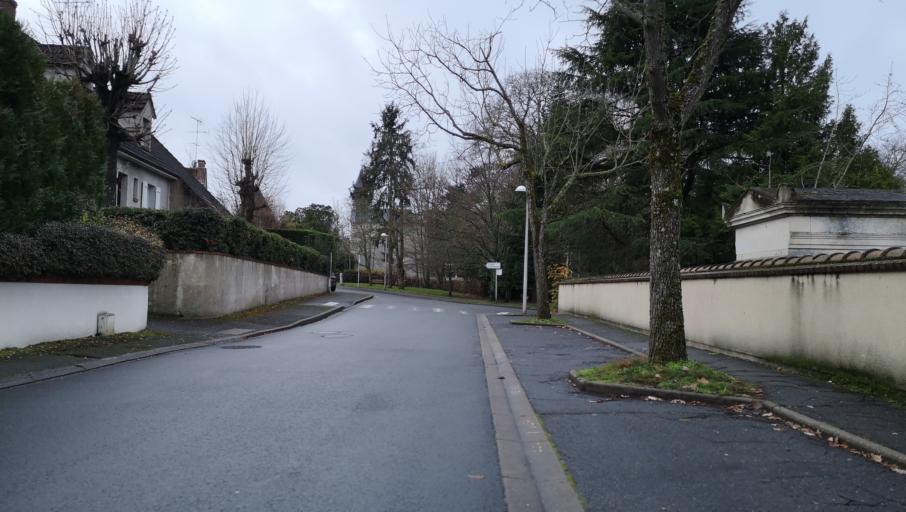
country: FR
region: Centre
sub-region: Departement du Loiret
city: Saint-Jean-de-Braye
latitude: 47.9055
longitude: 1.9653
